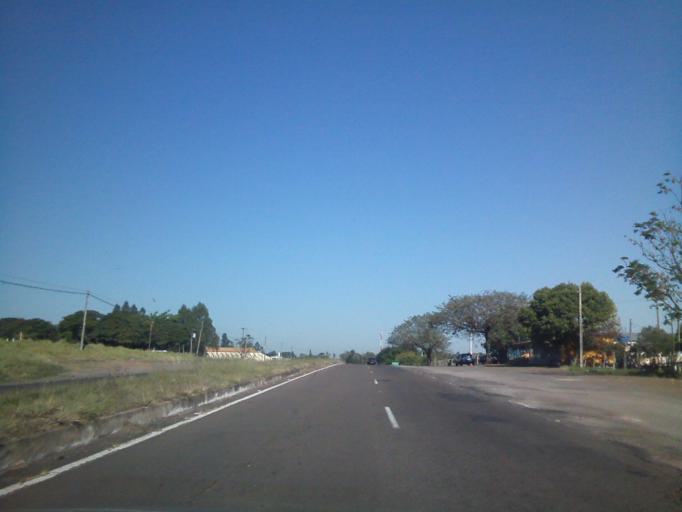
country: BR
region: Sao Paulo
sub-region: Presidente Prudente
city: Presidente Prudente
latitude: -22.1840
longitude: -51.4253
